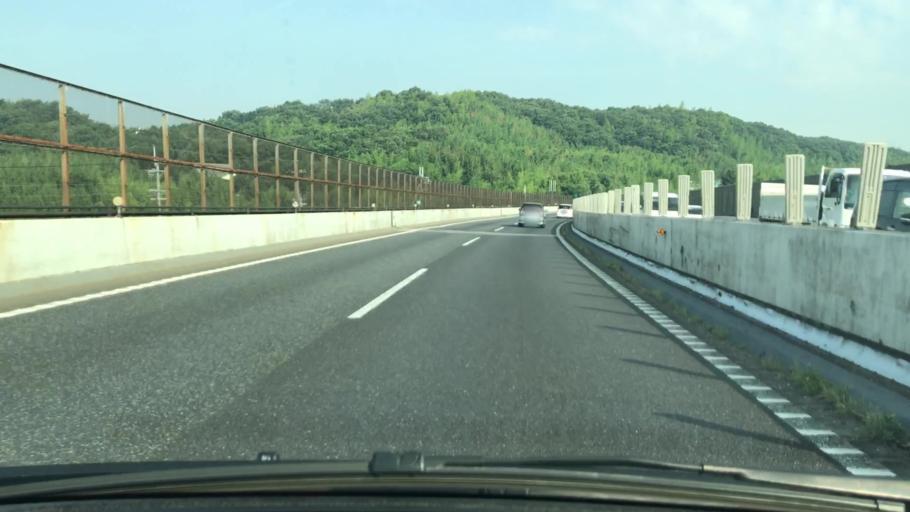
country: JP
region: Hyogo
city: Akashi
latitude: 34.6888
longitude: 134.9726
